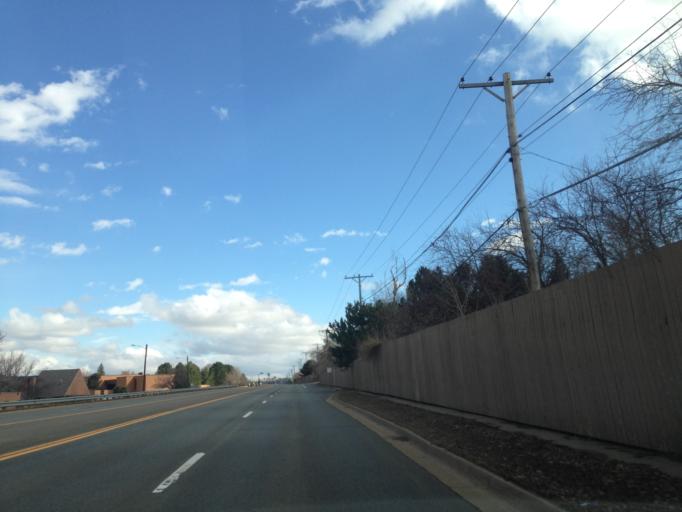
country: US
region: Colorado
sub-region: Boulder County
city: Boulder
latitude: 39.9791
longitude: -105.2443
